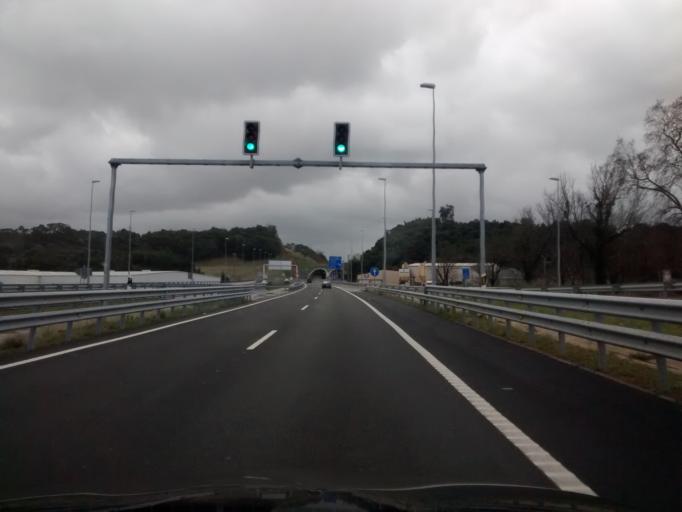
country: ES
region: Cantabria
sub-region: Provincia de Cantabria
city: Camargo
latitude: 43.4187
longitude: -3.8719
